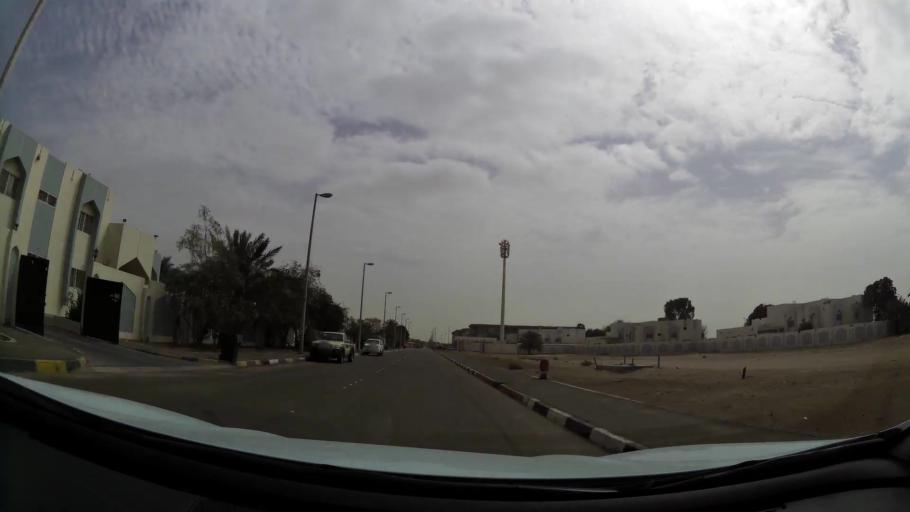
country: AE
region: Abu Dhabi
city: Abu Dhabi
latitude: 24.3938
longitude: 54.5102
